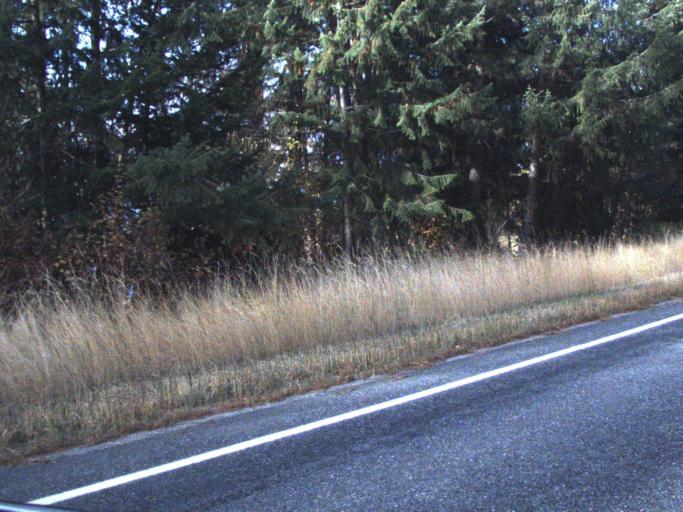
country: US
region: Washington
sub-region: Stevens County
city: Kettle Falls
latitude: 48.5266
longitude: -118.1363
